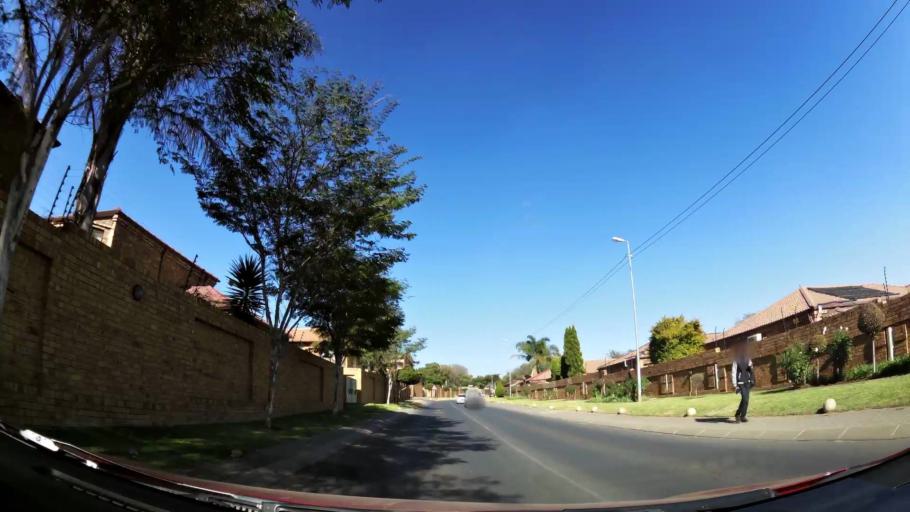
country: ZA
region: Gauteng
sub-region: City of Johannesburg Metropolitan Municipality
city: Diepsloot
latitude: -26.0517
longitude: 27.9680
